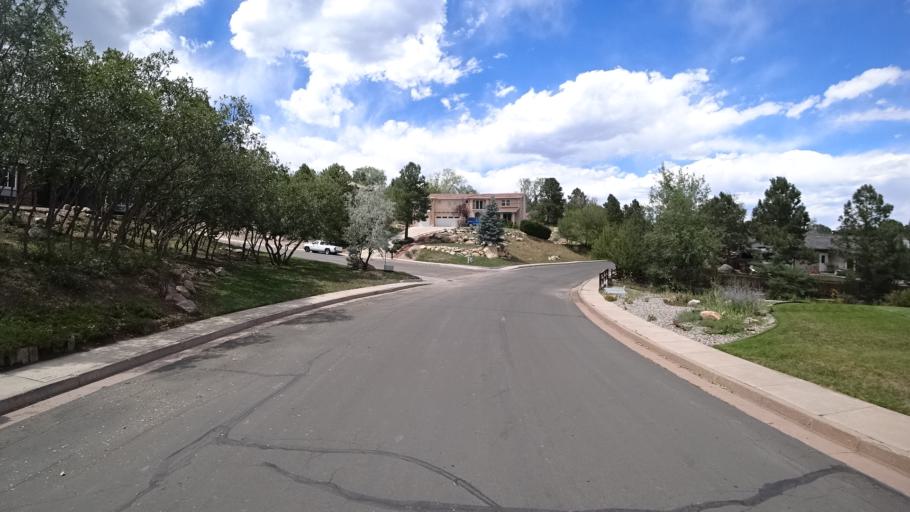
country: US
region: Colorado
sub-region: El Paso County
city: Stratmoor
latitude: 38.7713
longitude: -104.8311
